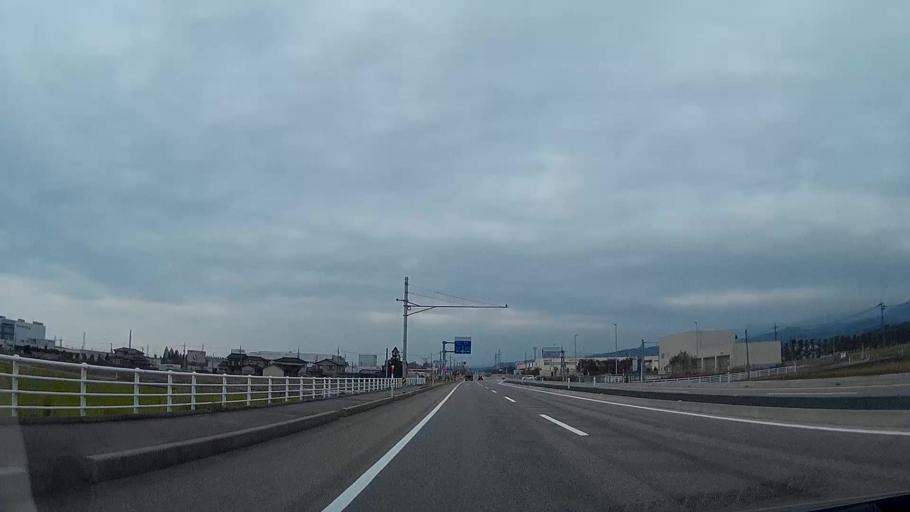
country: JP
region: Toyama
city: Uozu
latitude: 36.7753
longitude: 137.3893
